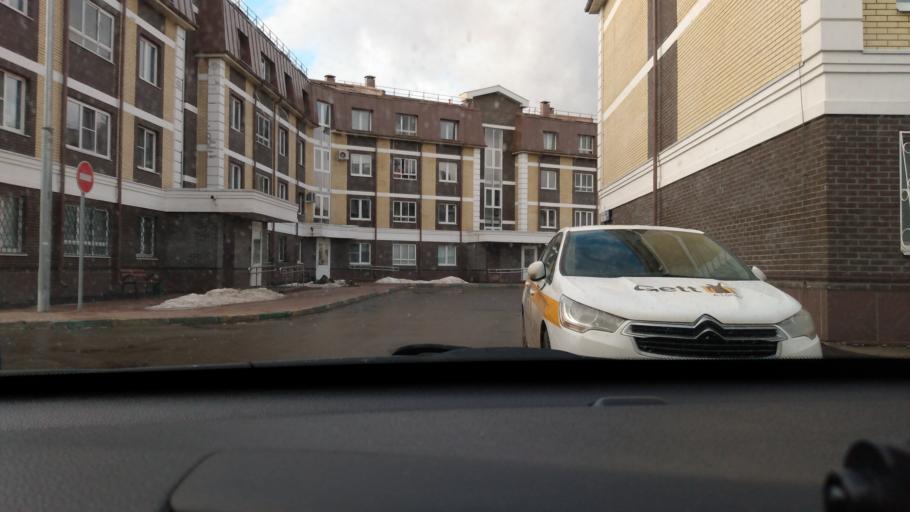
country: RU
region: Moskovskaya
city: Lesnyye Polyany
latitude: 55.9293
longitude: 37.8825
